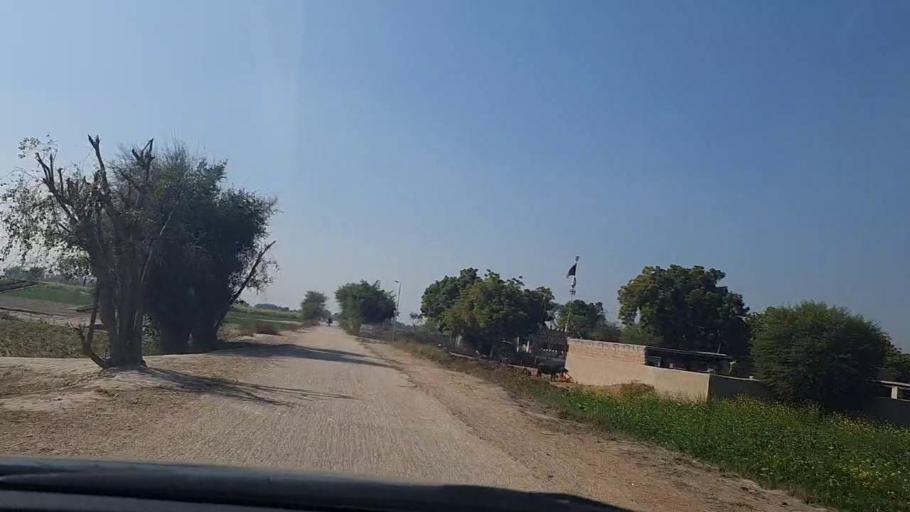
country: PK
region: Sindh
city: Daulatpur
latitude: 26.2846
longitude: 68.0595
